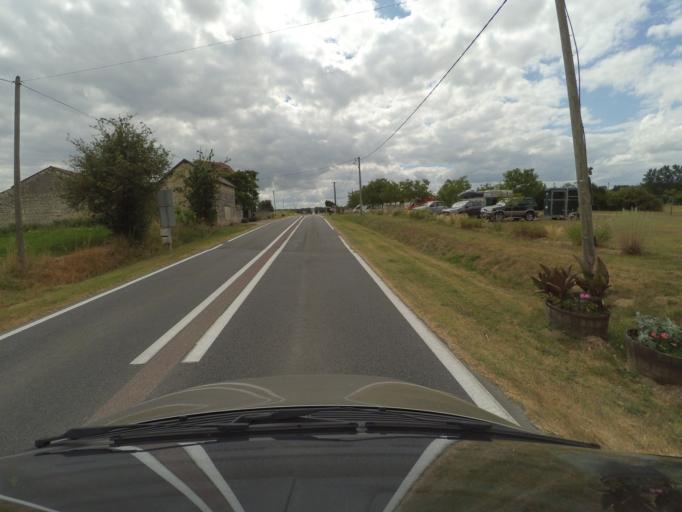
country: FR
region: Poitou-Charentes
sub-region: Departement de la Vienne
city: Saint-Gervais-les-Trois-Clochers
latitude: 46.9447
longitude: 0.4176
